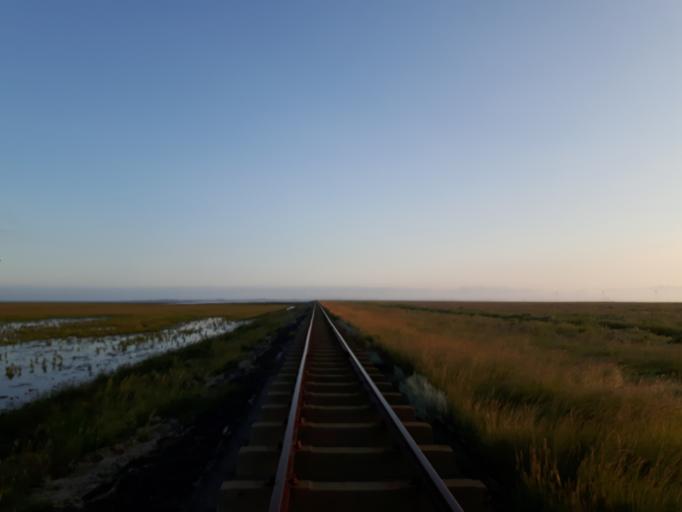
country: DE
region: Schleswig-Holstein
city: Dagebull
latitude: 54.6865
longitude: 8.7103
